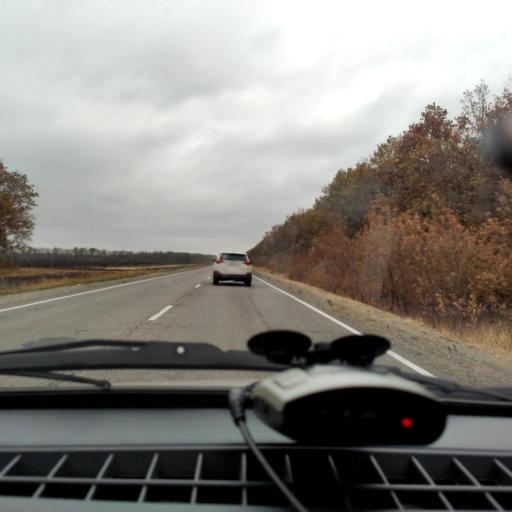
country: RU
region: Voronezj
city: Shilovo
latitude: 51.4195
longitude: 39.0067
